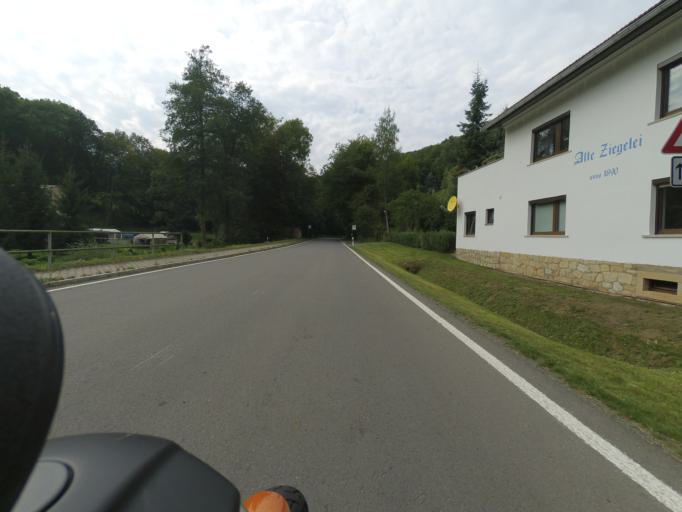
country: DE
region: Saxony
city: Dohna
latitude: 50.9115
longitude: 13.8732
